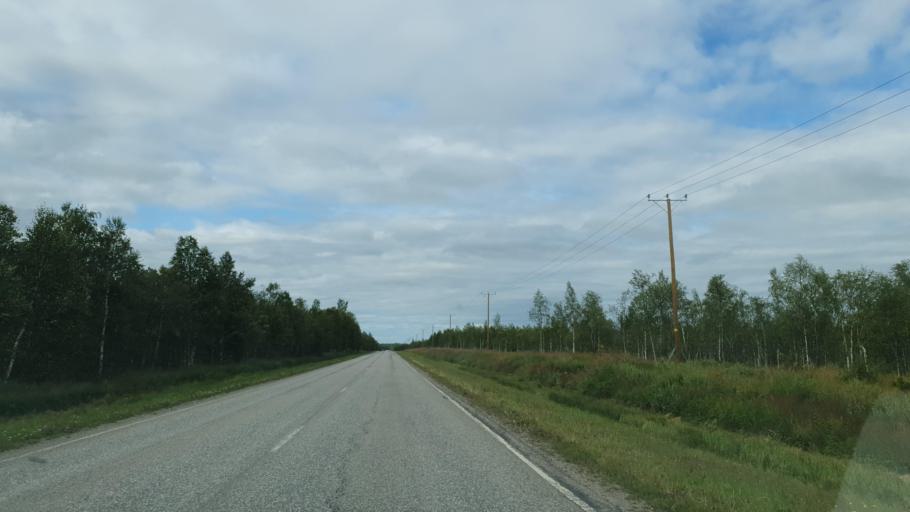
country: FI
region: Lapland
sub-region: Tunturi-Lappi
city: Kittilae
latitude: 67.6411
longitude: 25.1196
